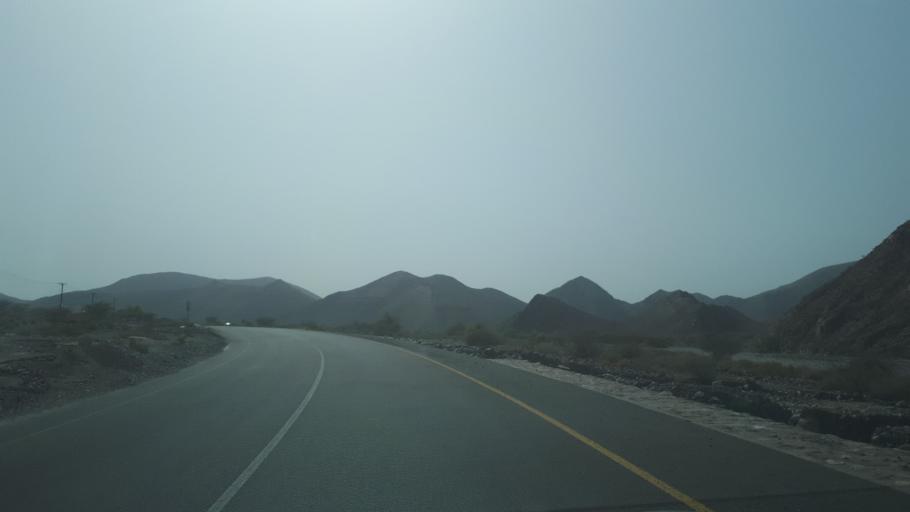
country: OM
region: Muhafazat ad Dakhiliyah
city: Bahla'
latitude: 23.2228
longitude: 56.9951
